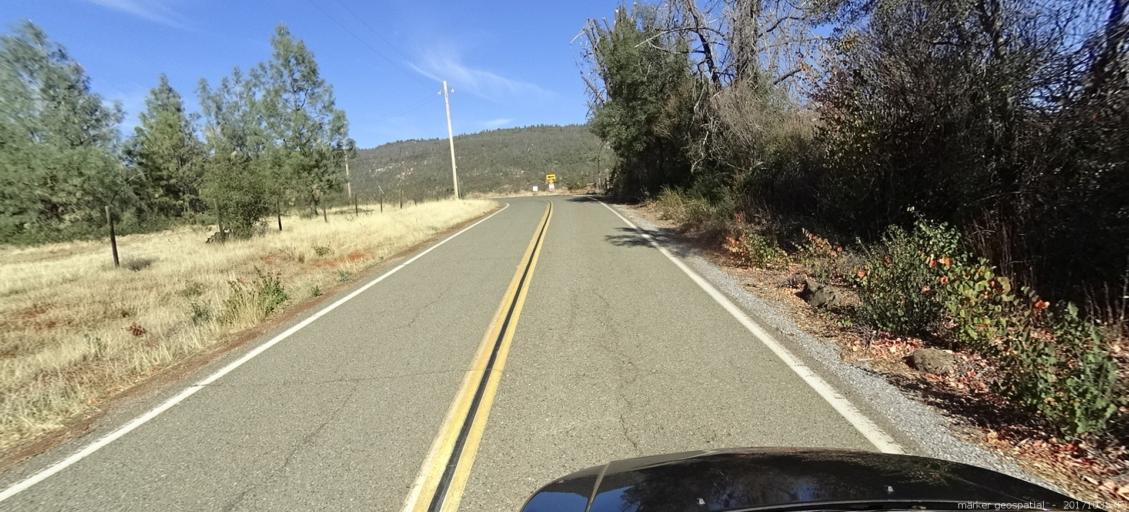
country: US
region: California
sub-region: Shasta County
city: Shingletown
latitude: 40.4492
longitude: -121.8759
